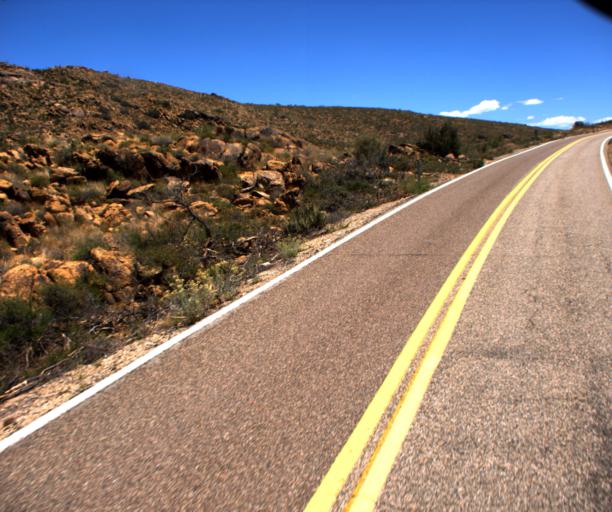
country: US
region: Arizona
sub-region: Yavapai County
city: Bagdad
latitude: 34.4456
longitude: -112.9570
